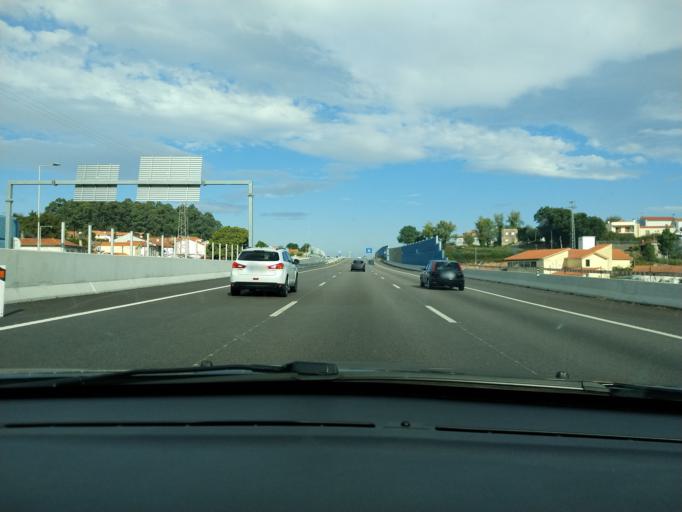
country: PT
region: Porto
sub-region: Vila Nova de Gaia
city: Perozinho
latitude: 41.0799
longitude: -8.5818
